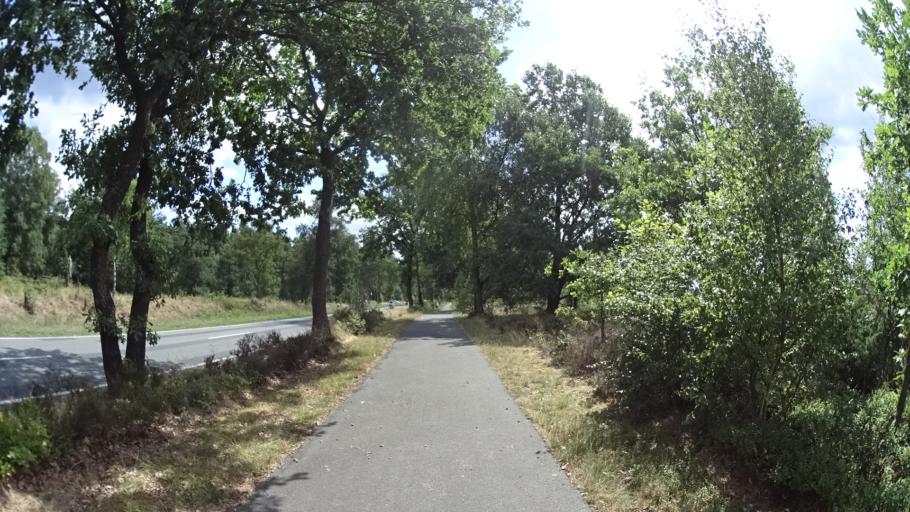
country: DE
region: Lower Saxony
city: Undeloh
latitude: 53.2136
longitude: 9.9495
